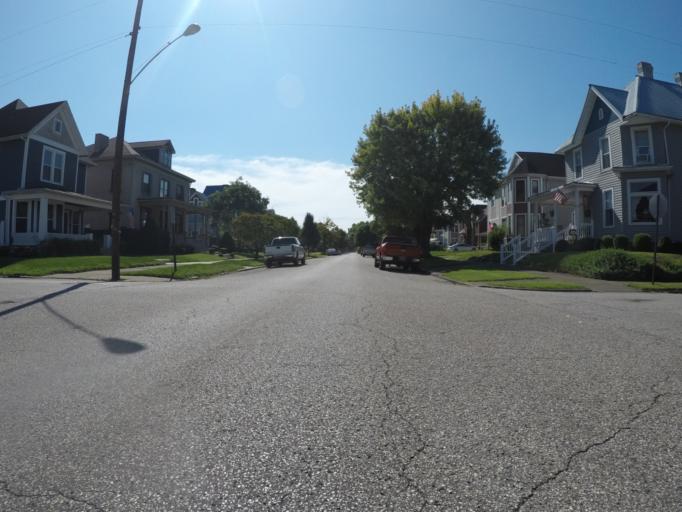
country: US
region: Ohio
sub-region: Lawrence County
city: Ironton
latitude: 38.5328
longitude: -82.6804
